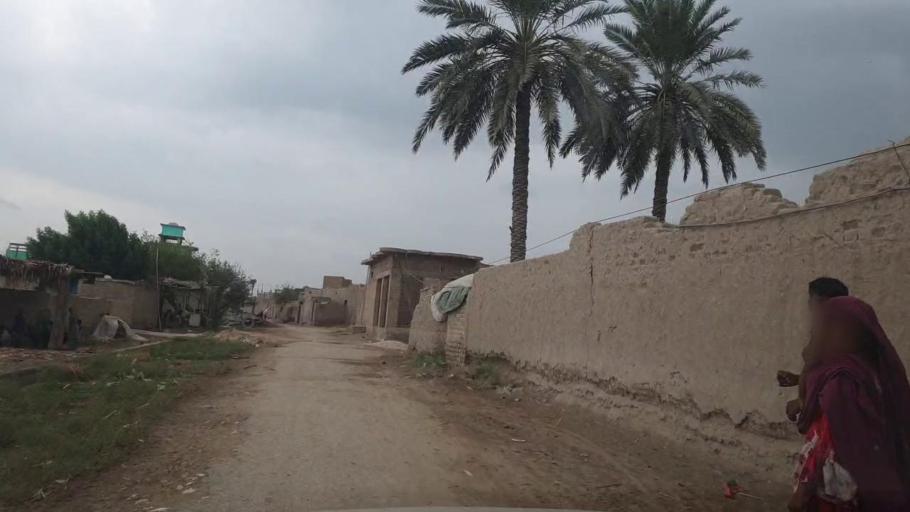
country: PK
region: Sindh
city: Khairpur
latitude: 27.5418
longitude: 68.7371
